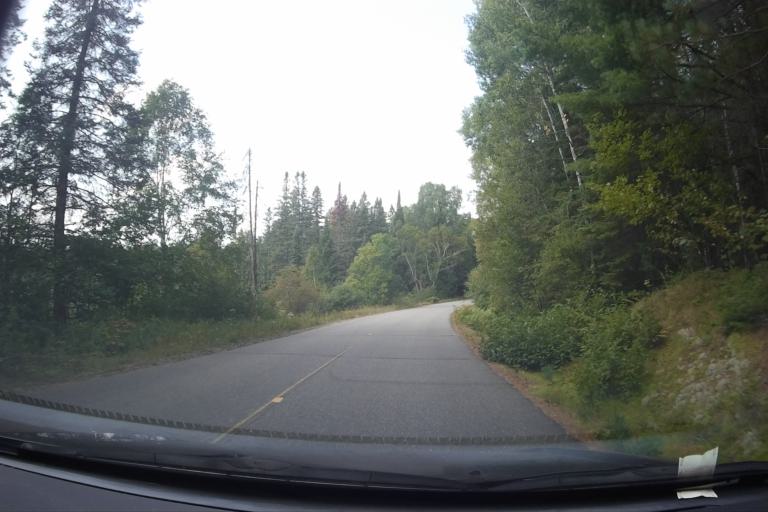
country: CA
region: Ontario
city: Bancroft
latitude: 45.6043
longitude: -78.3382
